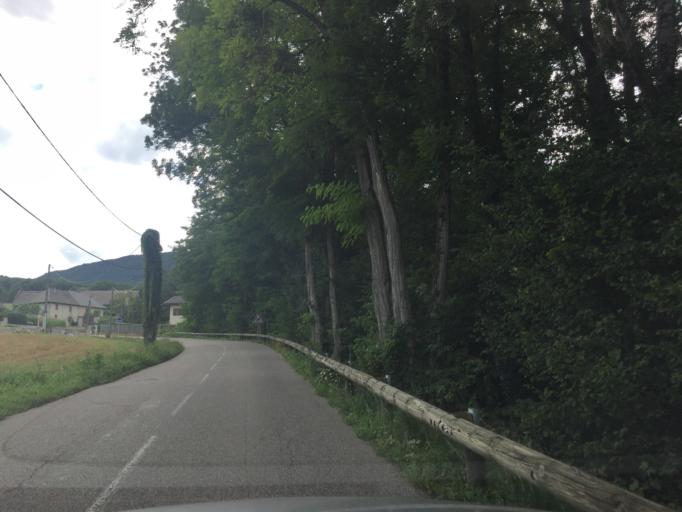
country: FR
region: Rhone-Alpes
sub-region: Departement de la Savoie
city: La Motte-Servolex
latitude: 45.5799
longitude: 5.8615
